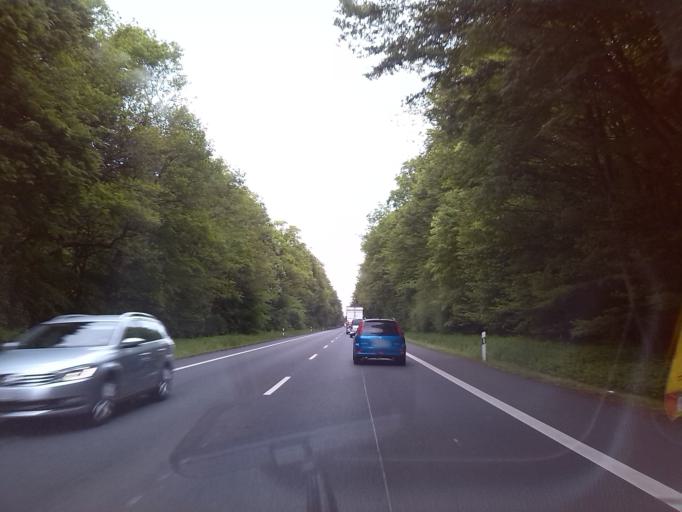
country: DE
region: Hesse
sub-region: Regierungsbezirk Darmstadt
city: Erzhausen
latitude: 49.9420
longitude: 8.6653
